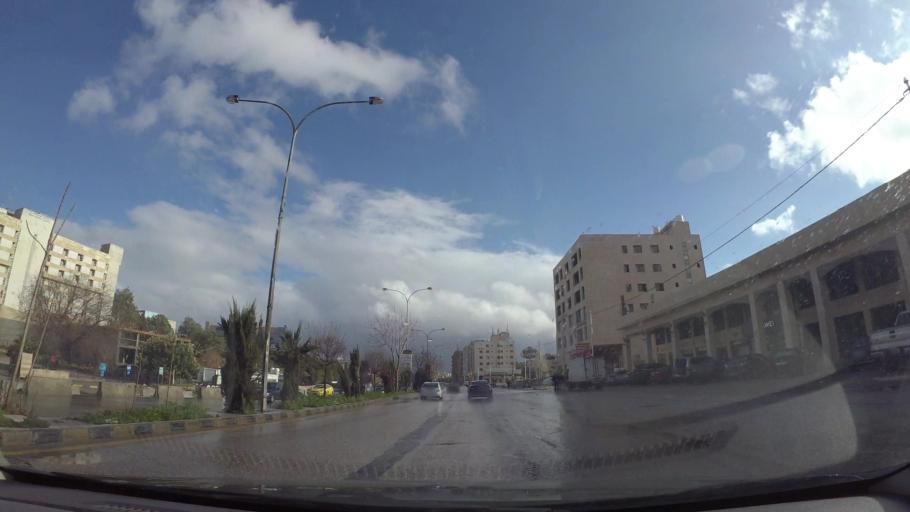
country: JO
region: Amman
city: Al Jubayhah
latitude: 32.0074
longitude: 35.8720
